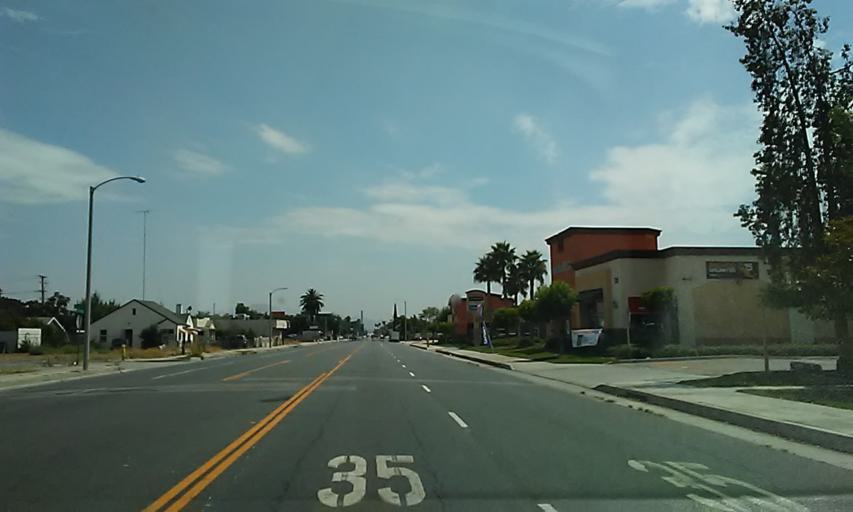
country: US
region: California
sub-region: San Bernardino County
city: San Bernardino
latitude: 34.1209
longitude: -117.3139
